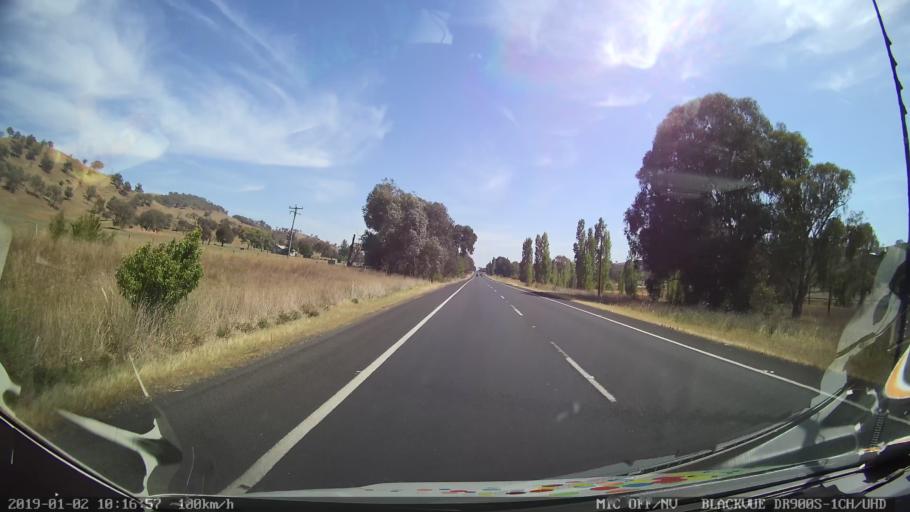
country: AU
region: New South Wales
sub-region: Gundagai
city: Gundagai
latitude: -35.0320
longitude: 148.1089
